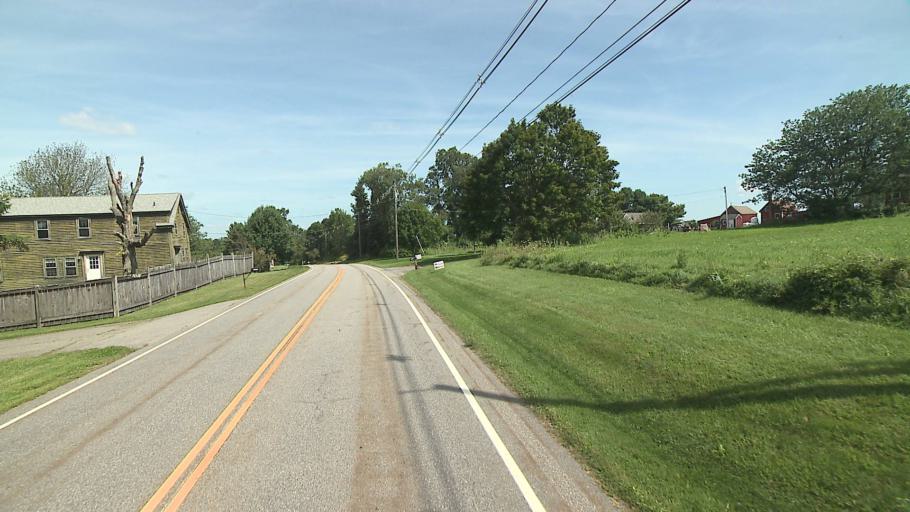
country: US
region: Connecticut
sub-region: Litchfield County
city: Bethlehem Village
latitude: 41.6744
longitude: -73.1968
